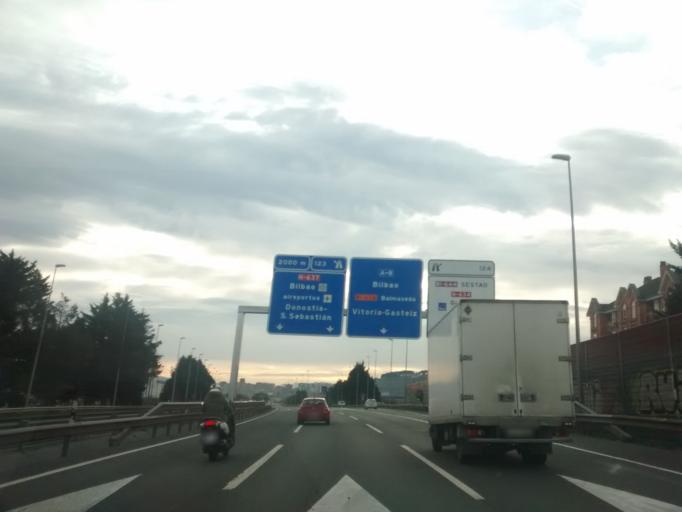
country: ES
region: Basque Country
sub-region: Bizkaia
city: Sestao
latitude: 43.2932
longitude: -3.0159
